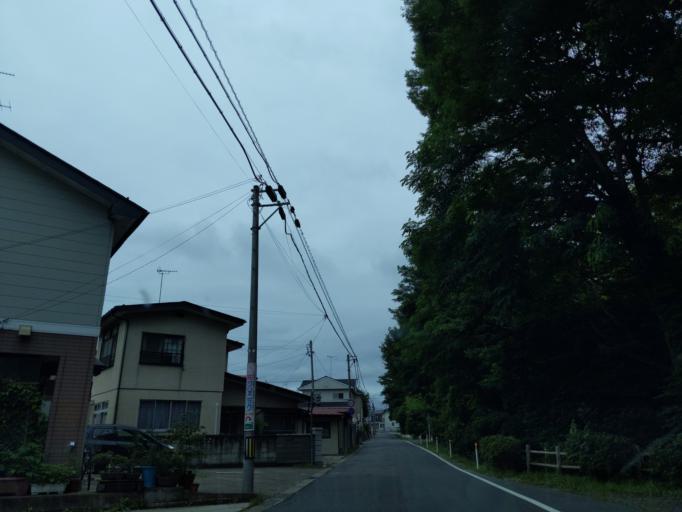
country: JP
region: Fukushima
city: Koriyama
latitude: 37.3785
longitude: 140.3612
